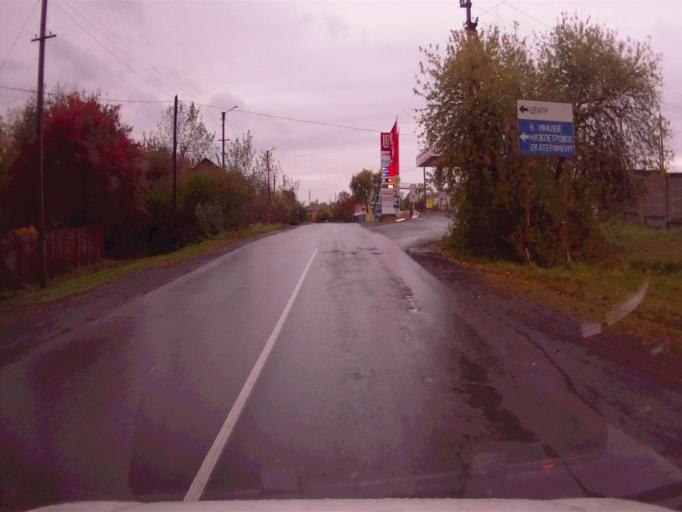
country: RU
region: Chelyabinsk
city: Verkhniy Ufaley
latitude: 56.0502
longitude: 60.2454
